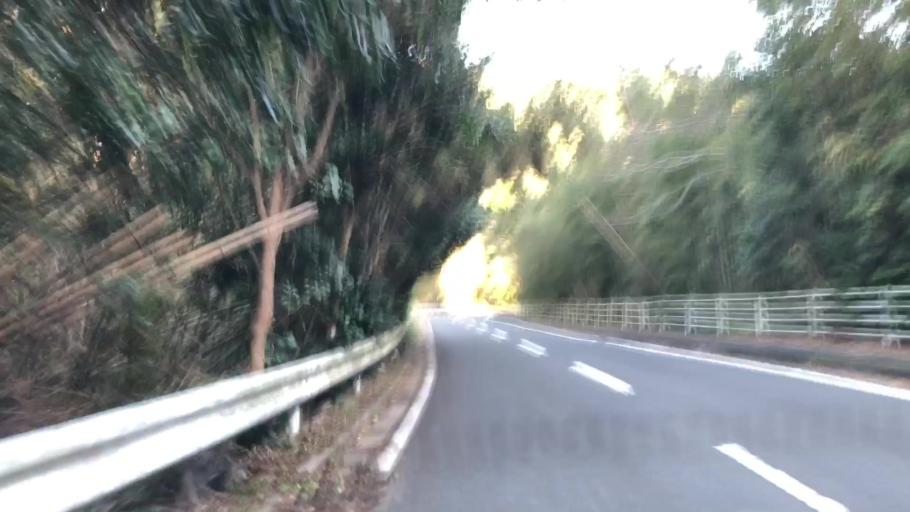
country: JP
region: Nagasaki
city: Sasebo
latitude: 33.0263
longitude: 129.6636
